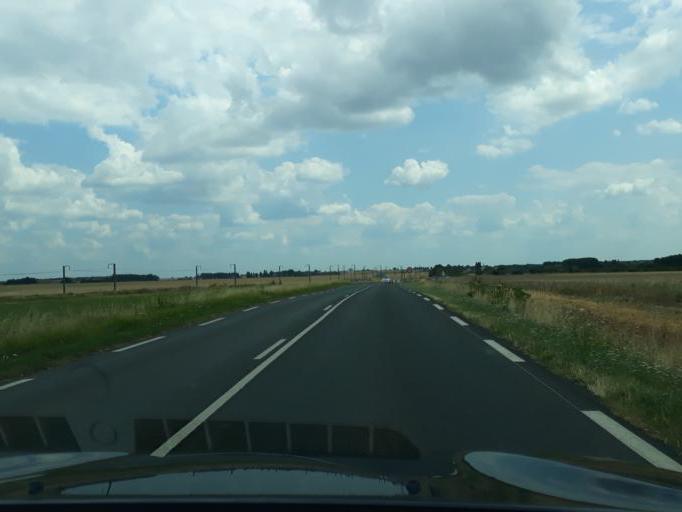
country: FR
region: Centre
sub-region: Departement du Cher
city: Baugy
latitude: 47.0139
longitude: 2.7203
